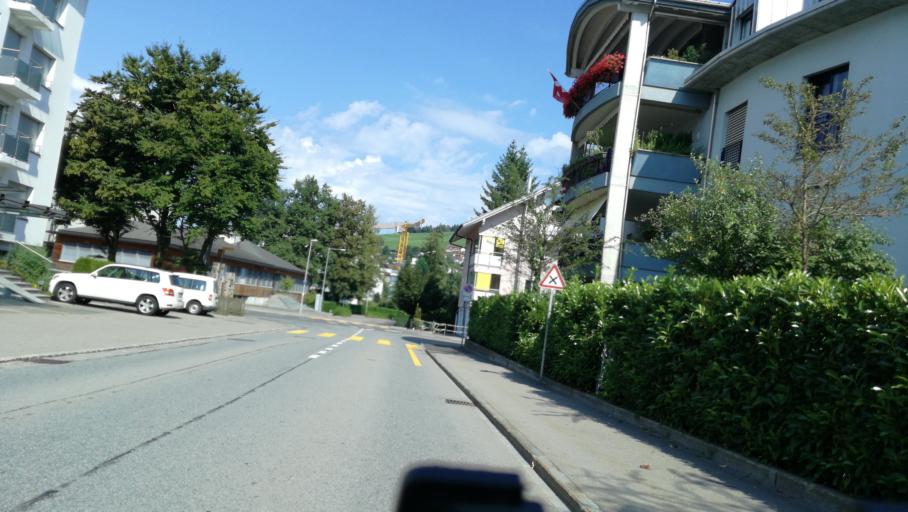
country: CH
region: Zug
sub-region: Zug
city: Unterageri
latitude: 47.1354
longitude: 8.5805
